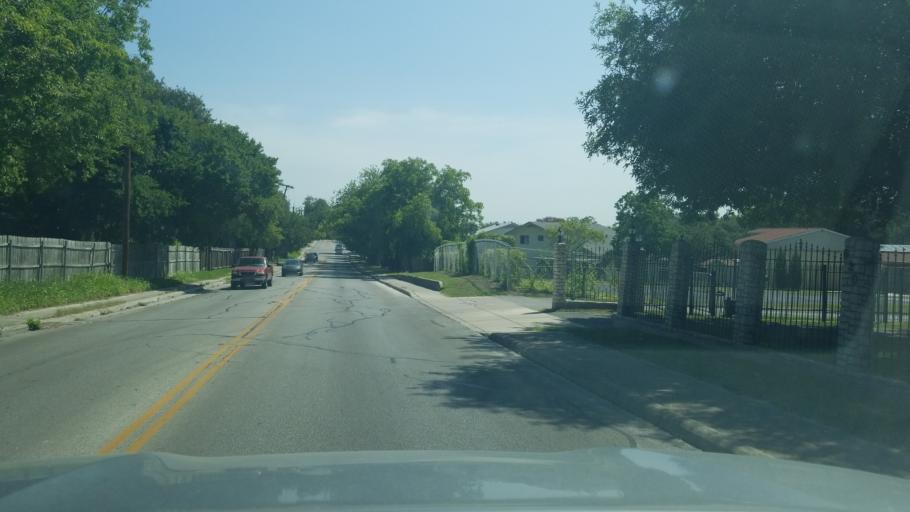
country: US
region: Texas
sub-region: Bexar County
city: Hollywood Park
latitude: 29.5720
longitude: -98.4714
